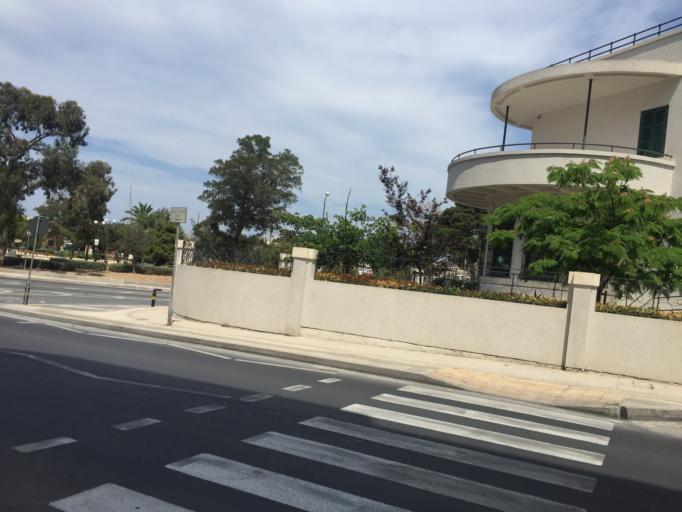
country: MT
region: Ta' Xbiex
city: Ta' Xbiex
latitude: 35.9013
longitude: 14.4946
